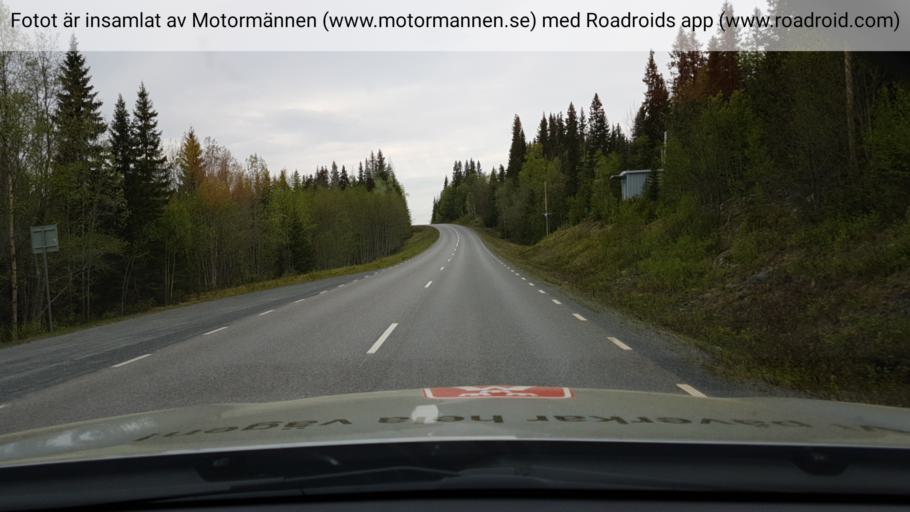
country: SE
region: Jaemtland
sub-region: Are Kommun
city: Are
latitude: 63.5069
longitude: 13.1483
